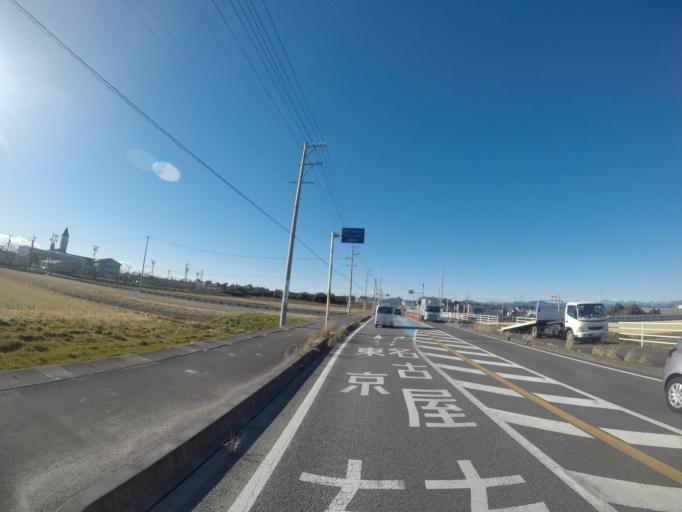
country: JP
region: Shizuoka
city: Fujieda
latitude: 34.8154
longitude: 138.2675
